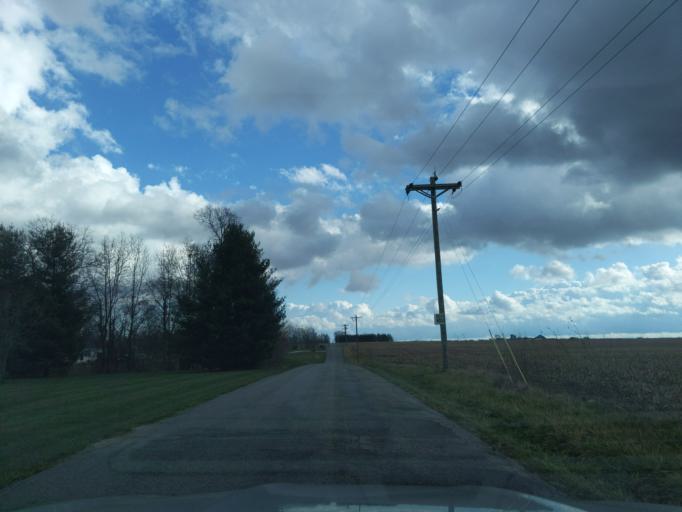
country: US
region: Indiana
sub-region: Decatur County
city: Saint Paul
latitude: 39.4093
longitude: -85.5585
